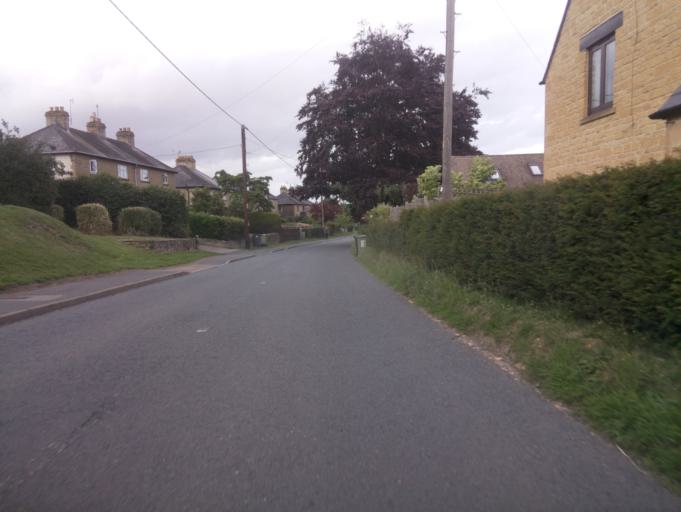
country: GB
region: England
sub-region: Gloucestershire
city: Chipping Campden
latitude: 52.0159
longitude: -1.7570
